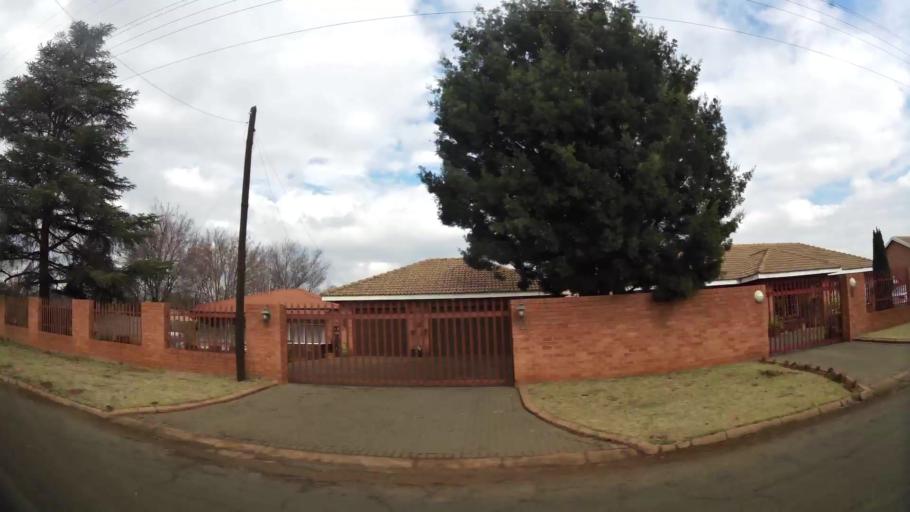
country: ZA
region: Gauteng
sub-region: Sedibeng District Municipality
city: Meyerton
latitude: -26.5864
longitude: 28.0136
